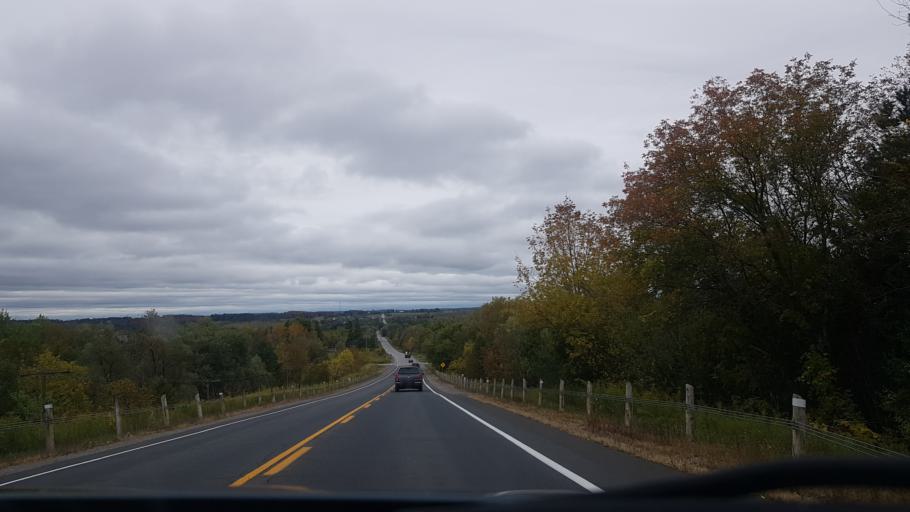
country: CA
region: Ontario
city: Omemee
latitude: 44.2141
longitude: -78.4747
